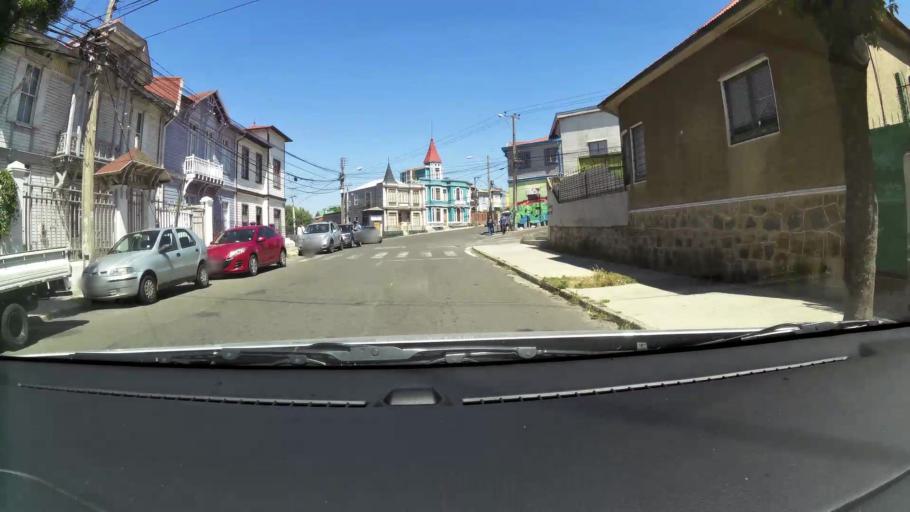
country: CL
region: Valparaiso
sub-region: Provincia de Valparaiso
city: Valparaiso
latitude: -33.0275
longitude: -71.6342
